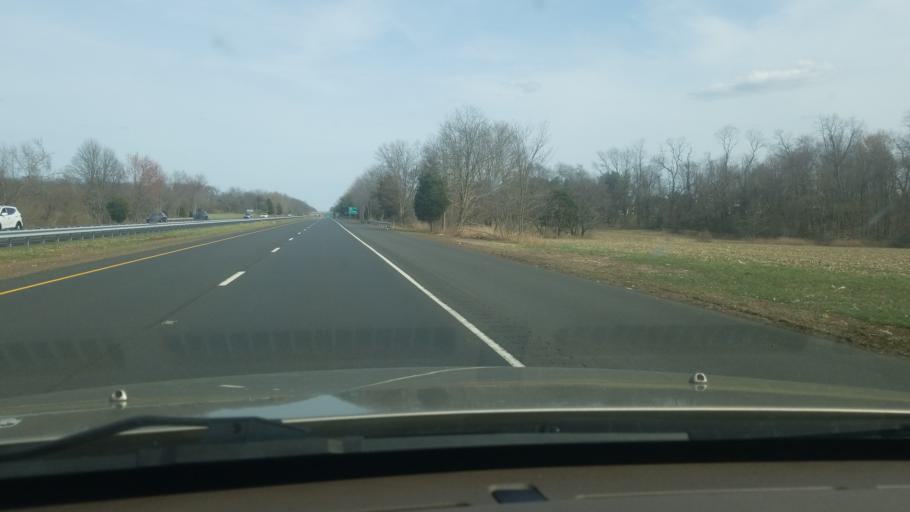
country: US
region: New Jersey
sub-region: Monmouth County
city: West Freehold
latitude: 40.2531
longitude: -74.3266
